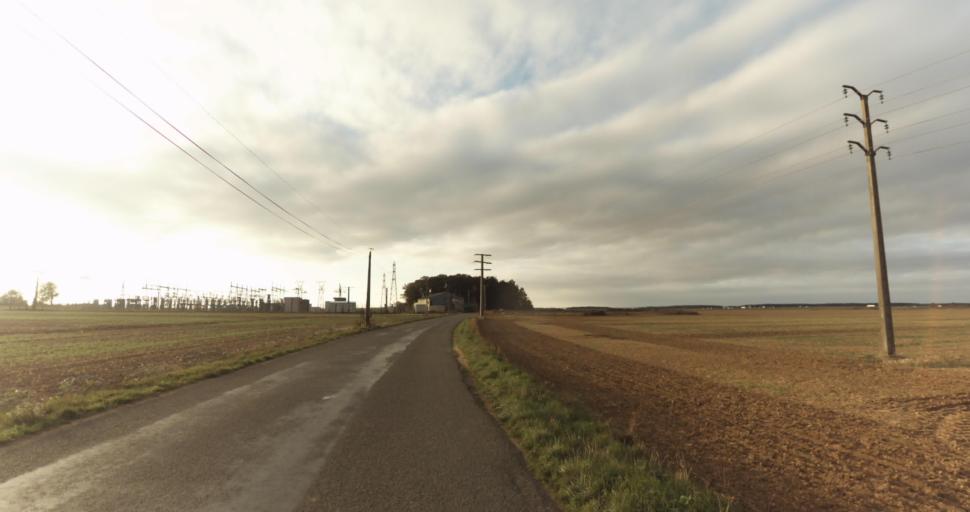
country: FR
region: Centre
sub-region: Departement d'Eure-et-Loir
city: Vernouillet
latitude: 48.7114
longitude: 1.3817
